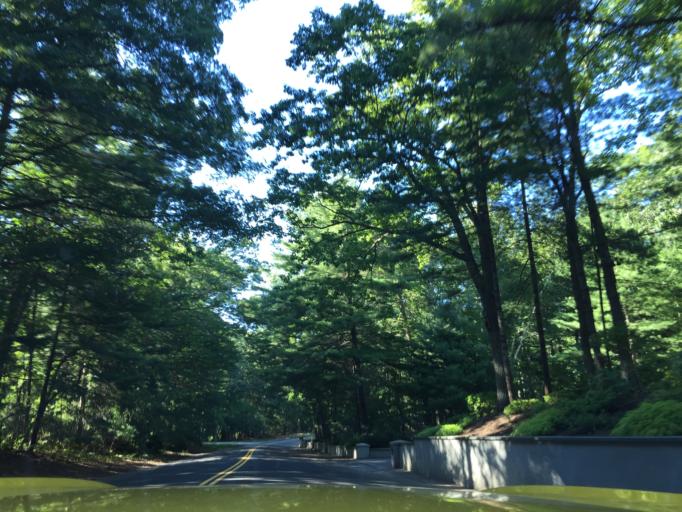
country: US
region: New York
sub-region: Suffolk County
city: Southold
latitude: 41.0413
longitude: -72.3916
